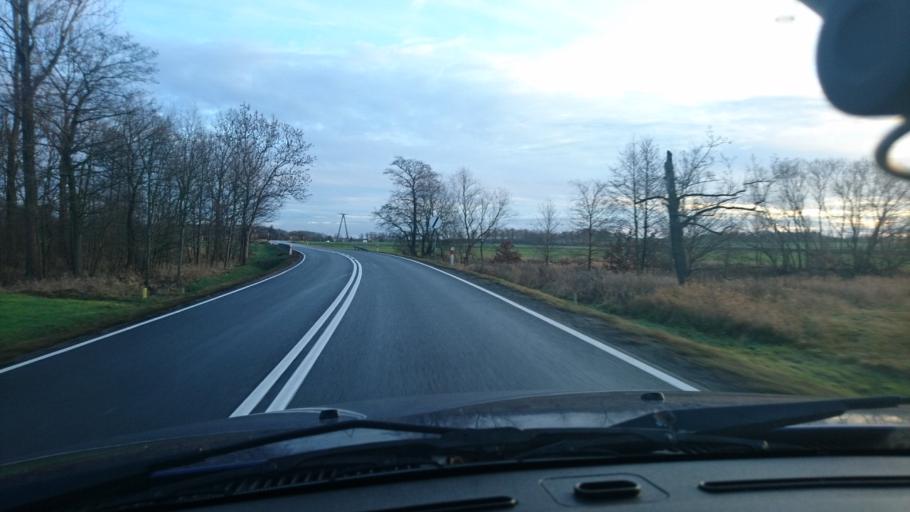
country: PL
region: Opole Voivodeship
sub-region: Powiat kluczborski
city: Byczyna
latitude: 51.1442
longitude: 18.1917
